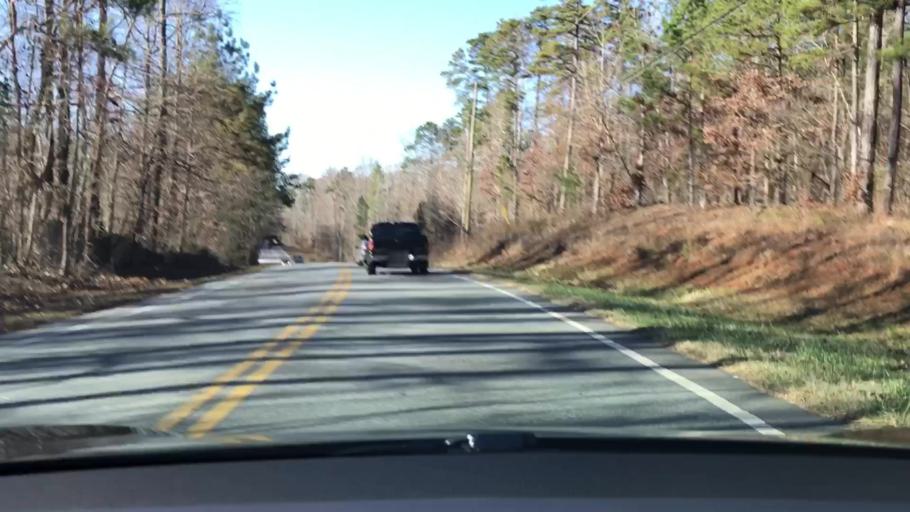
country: US
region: Georgia
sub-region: Barrow County
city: Auburn
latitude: 34.0983
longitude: -83.8673
